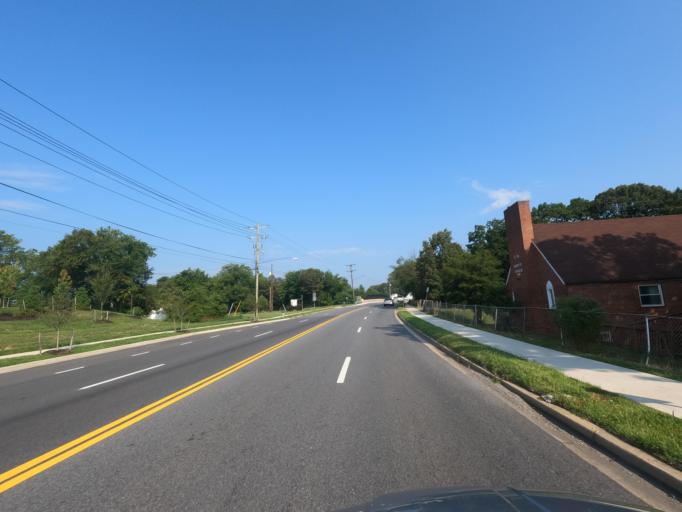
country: US
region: Maryland
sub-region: Prince George's County
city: Temple Hills
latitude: 38.8162
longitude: -76.9475
